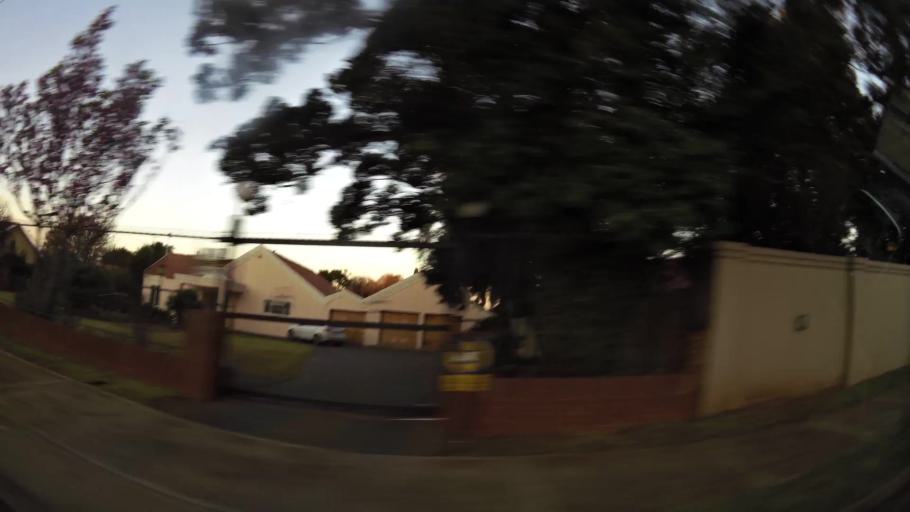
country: ZA
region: Gauteng
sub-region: City of Johannesburg Metropolitan Municipality
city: Roodepoort
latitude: -26.1646
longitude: 27.9170
